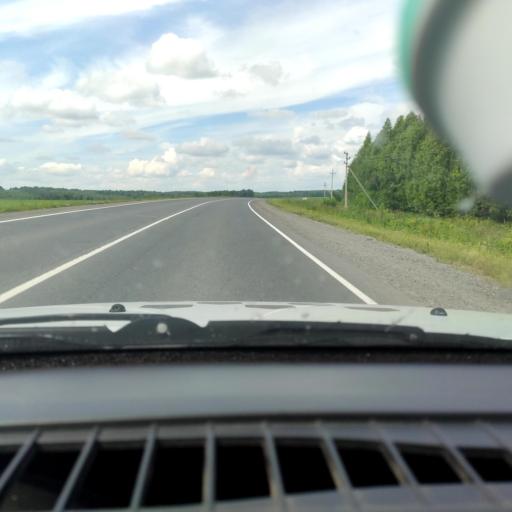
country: RU
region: Perm
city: Verkhnechusovskiye Gorodki
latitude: 58.2174
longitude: 57.1082
